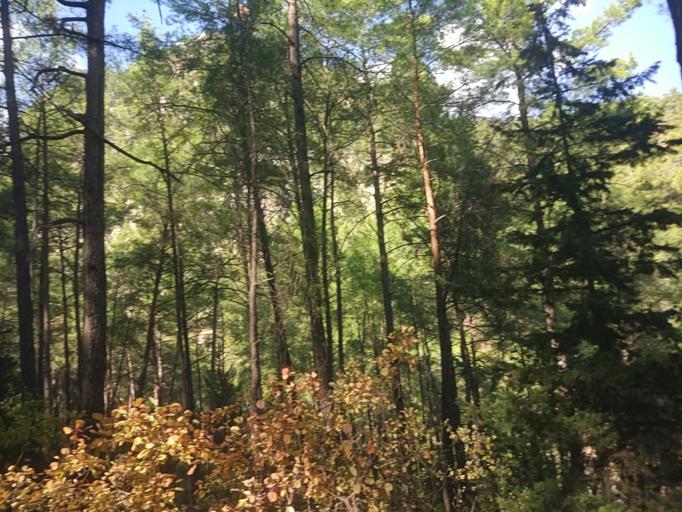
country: TR
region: Antalya
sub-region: Kemer
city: Goeynuek
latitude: 36.6781
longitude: 30.4924
